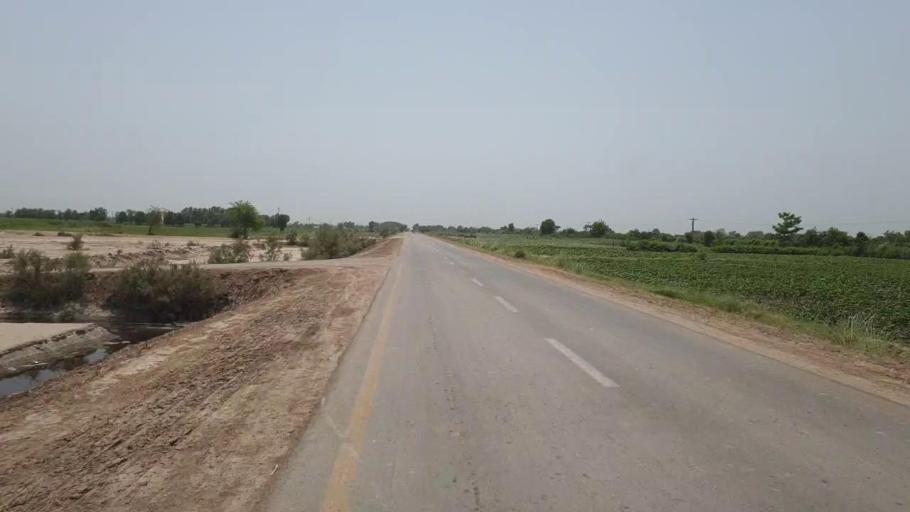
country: PK
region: Sindh
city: Moro
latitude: 26.5976
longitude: 68.1136
